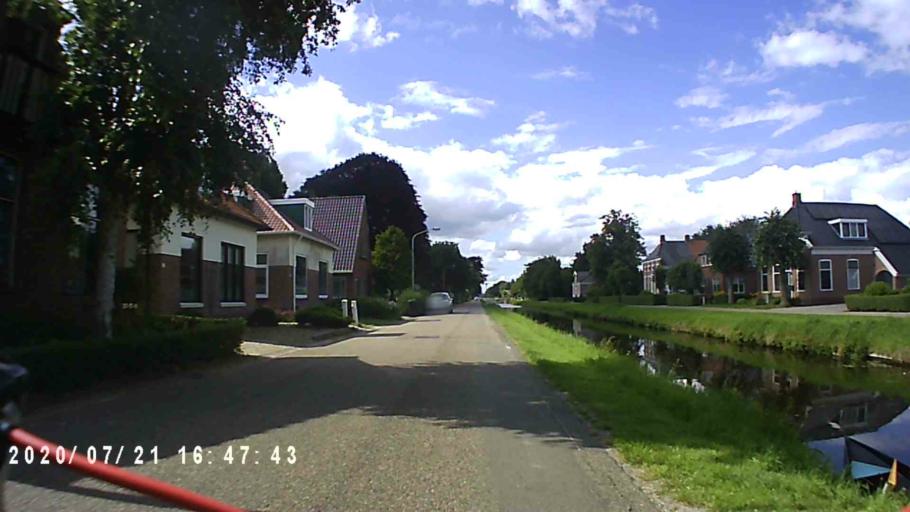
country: NL
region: Groningen
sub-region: Gemeente Hoogezand-Sappemeer
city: Hoogezand
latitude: 53.1144
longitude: 6.7777
